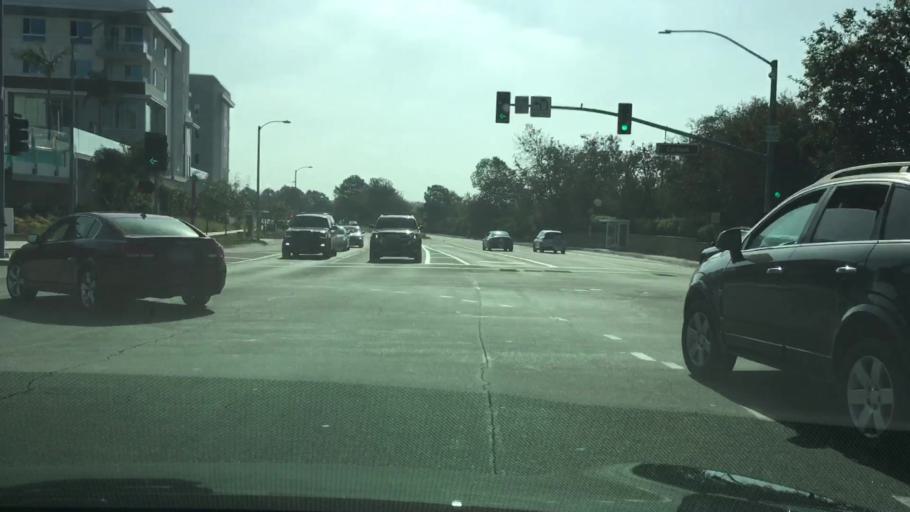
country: US
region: California
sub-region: Orange County
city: Irvine
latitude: 33.6712
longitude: -117.8451
